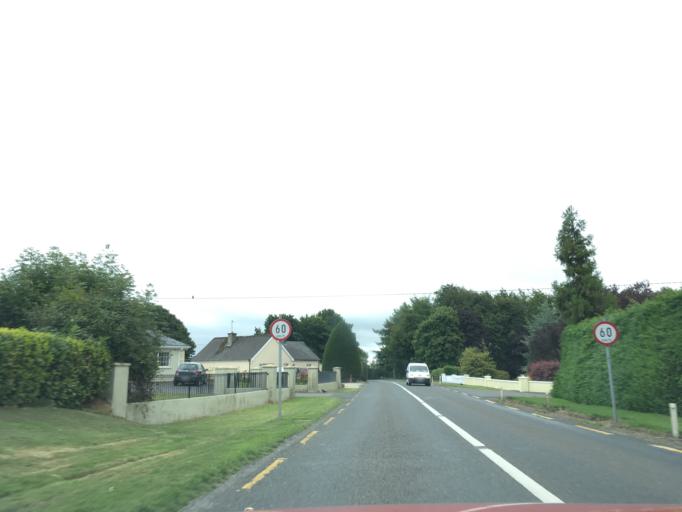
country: IE
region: Munster
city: Cashel
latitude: 52.4656
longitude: -7.8311
